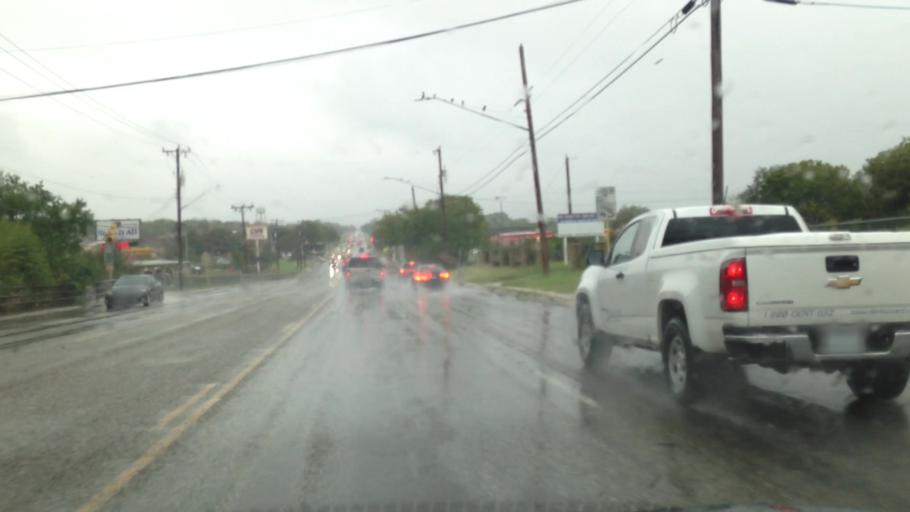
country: US
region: Texas
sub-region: Bexar County
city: Live Oak
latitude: 29.5757
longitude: -98.3709
